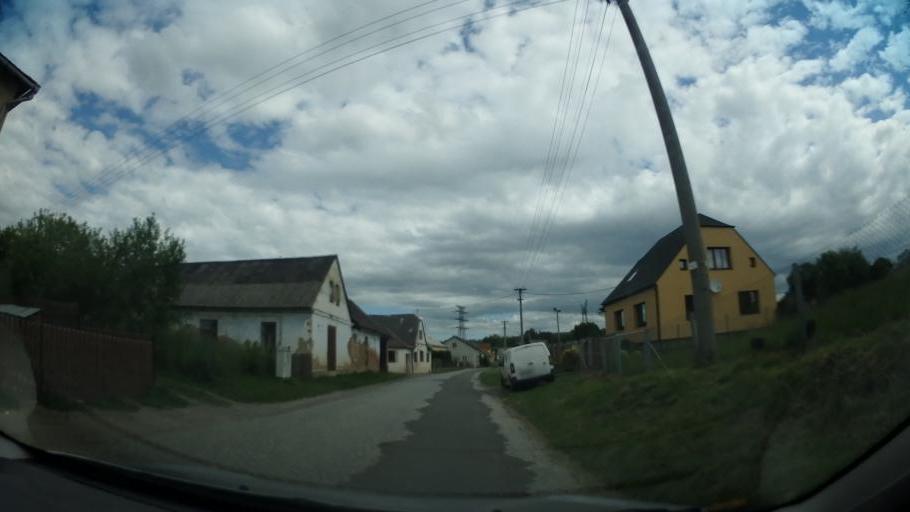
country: CZ
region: Pardubicky
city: Kuncina
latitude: 49.8444
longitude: 16.6973
